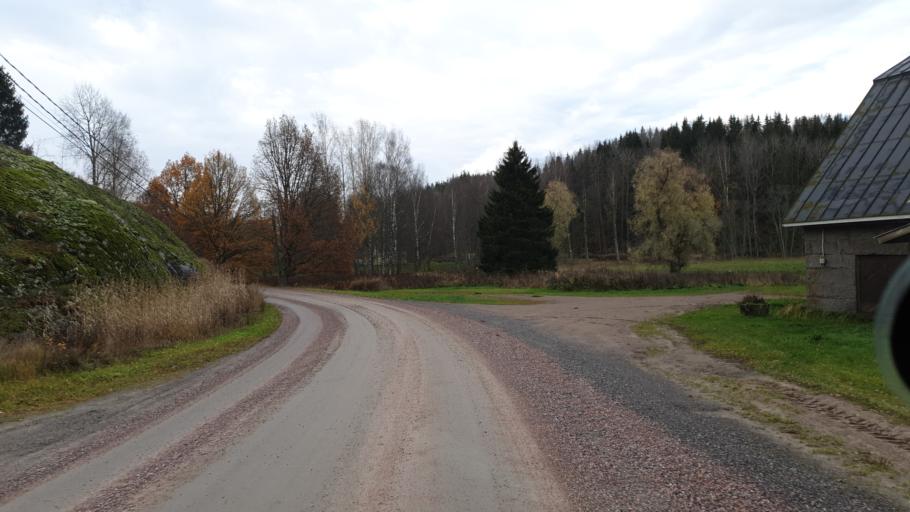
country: FI
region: Uusimaa
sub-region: Helsinki
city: Siuntio
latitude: 60.1433
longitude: 24.2609
